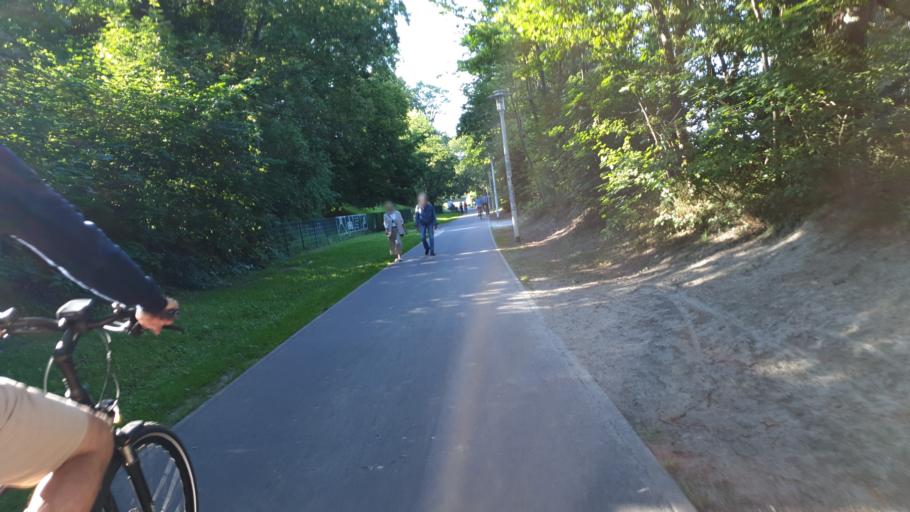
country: DE
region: Mecklenburg-Vorpommern
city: Stralsund
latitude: 54.3281
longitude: 13.0837
